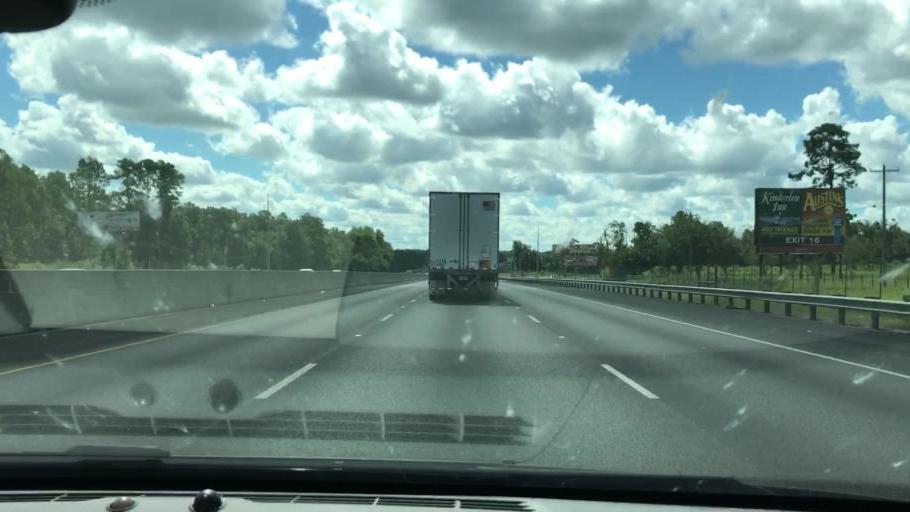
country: US
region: Georgia
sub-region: Lowndes County
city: Remerton
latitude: 30.8799
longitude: -83.3458
